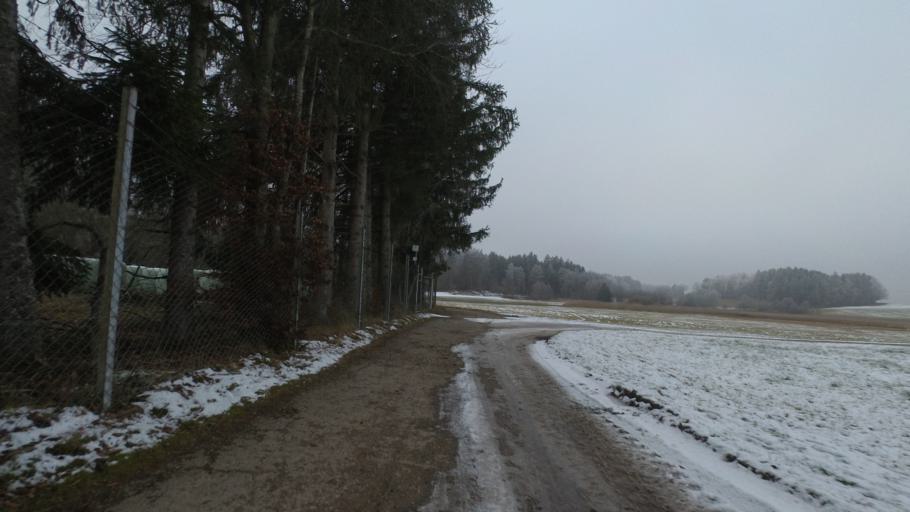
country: DE
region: Bavaria
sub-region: Upper Bavaria
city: Nussdorf
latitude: 47.8850
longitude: 12.5718
